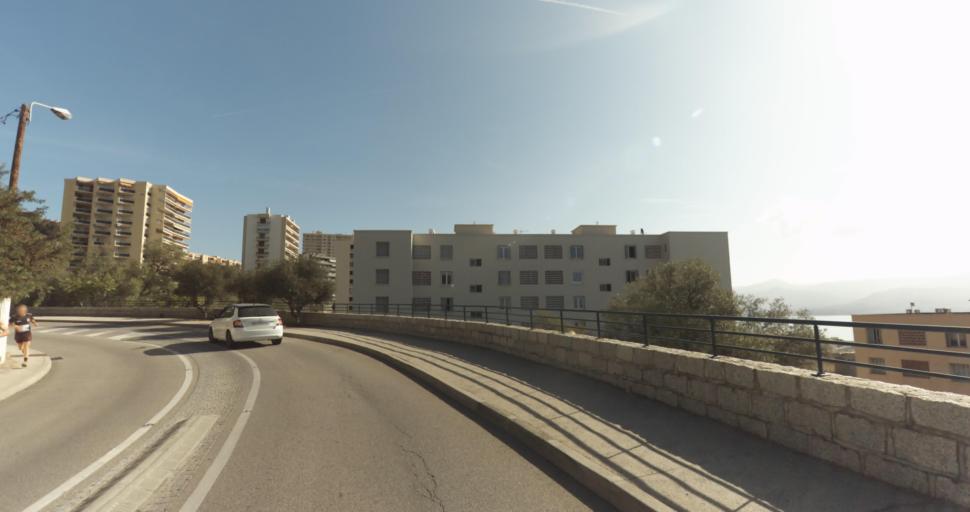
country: FR
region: Corsica
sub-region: Departement de la Corse-du-Sud
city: Ajaccio
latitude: 41.9184
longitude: 8.7266
